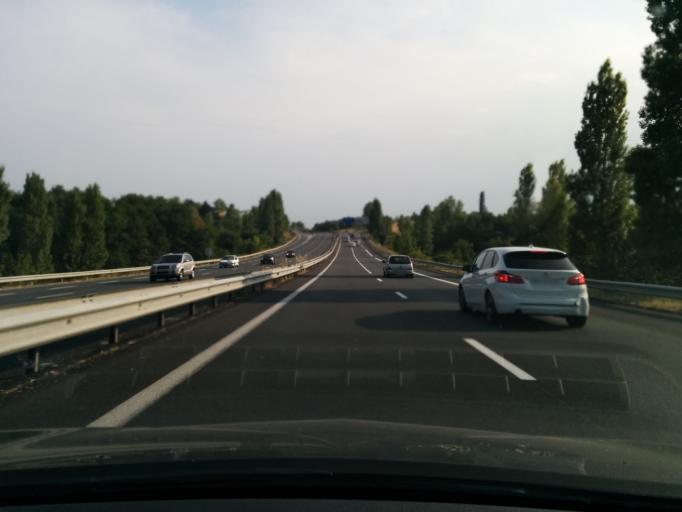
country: FR
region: Midi-Pyrenees
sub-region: Departement de la Haute-Garonne
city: Garidech
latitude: 43.7215
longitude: 1.5684
